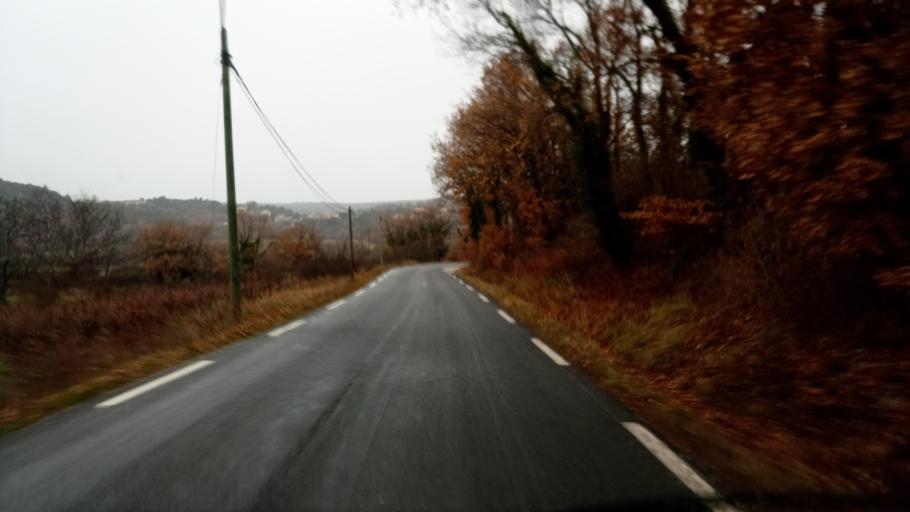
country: FR
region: Provence-Alpes-Cote d'Azur
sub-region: Departement du Var
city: Saint-Julien
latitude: 43.6964
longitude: 5.9008
